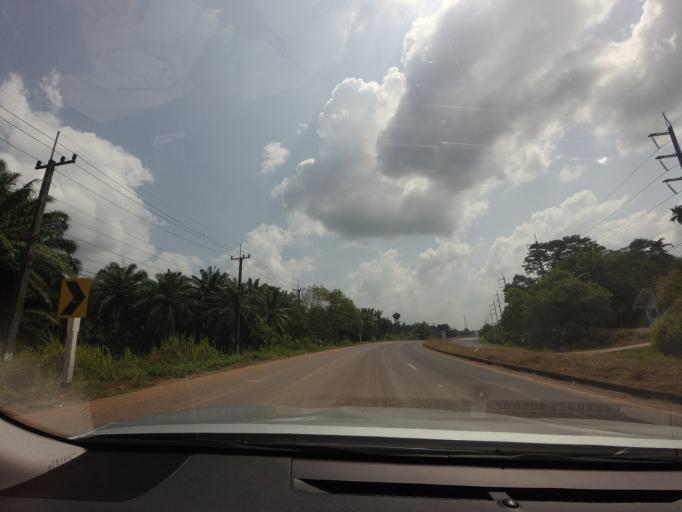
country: TH
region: Phangnga
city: Thap Put
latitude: 8.5070
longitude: 98.6904
